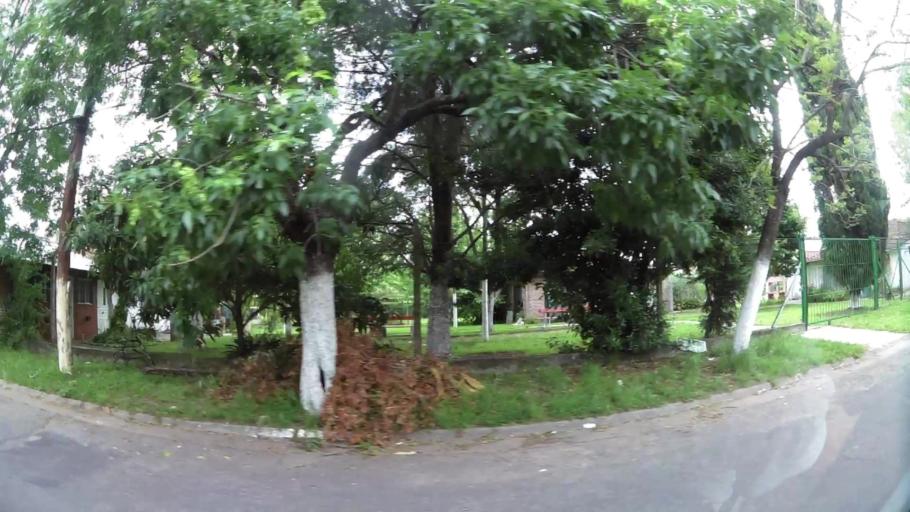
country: AR
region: Buenos Aires
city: San Justo
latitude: -34.7355
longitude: -58.5293
